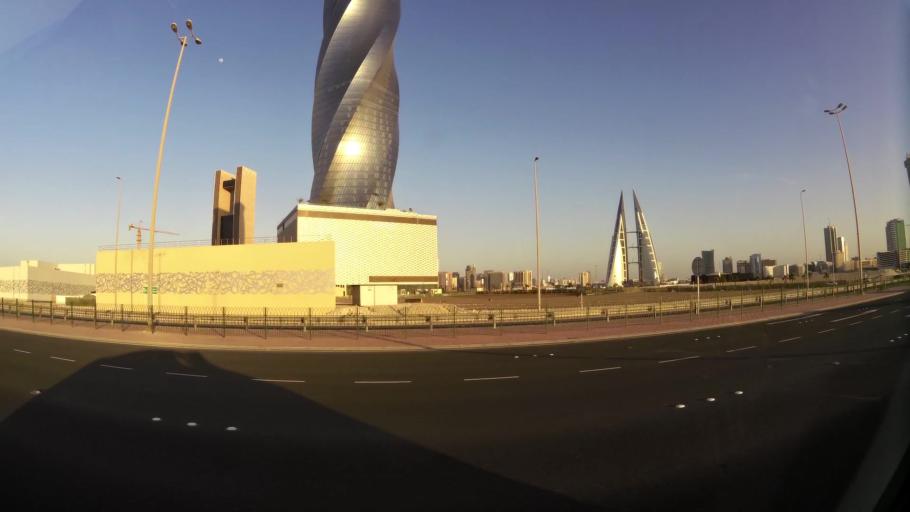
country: BH
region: Manama
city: Manama
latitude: 26.2471
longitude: 50.5748
